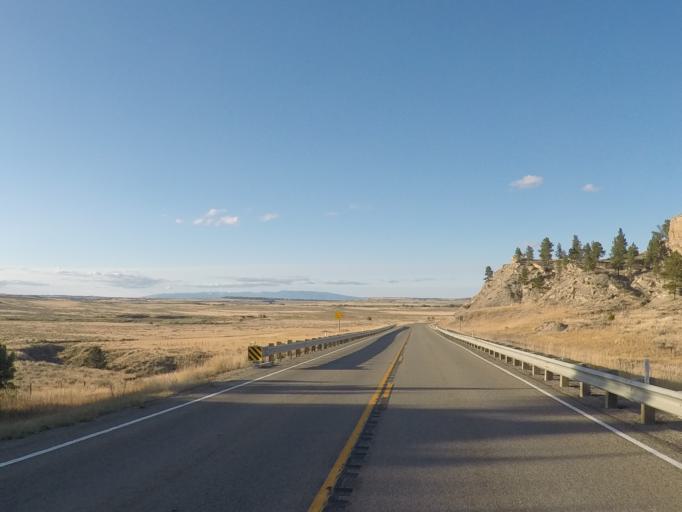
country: US
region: Montana
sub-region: Golden Valley County
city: Ryegate
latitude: 46.2688
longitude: -108.9391
